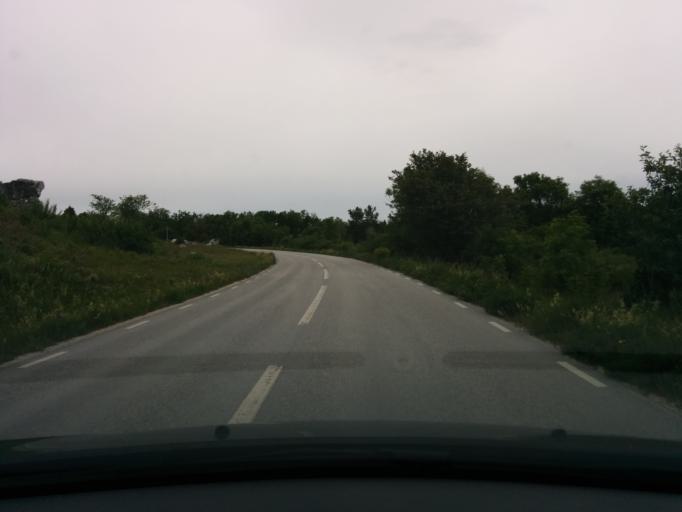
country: SE
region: Gotland
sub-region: Gotland
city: Slite
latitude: 57.6698
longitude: 18.7752
